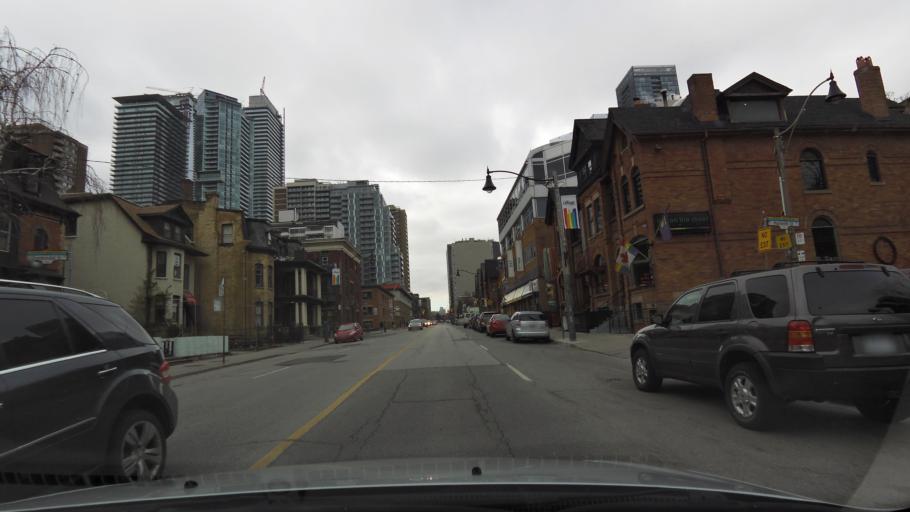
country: CA
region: Ontario
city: Toronto
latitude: 43.6667
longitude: -79.3813
